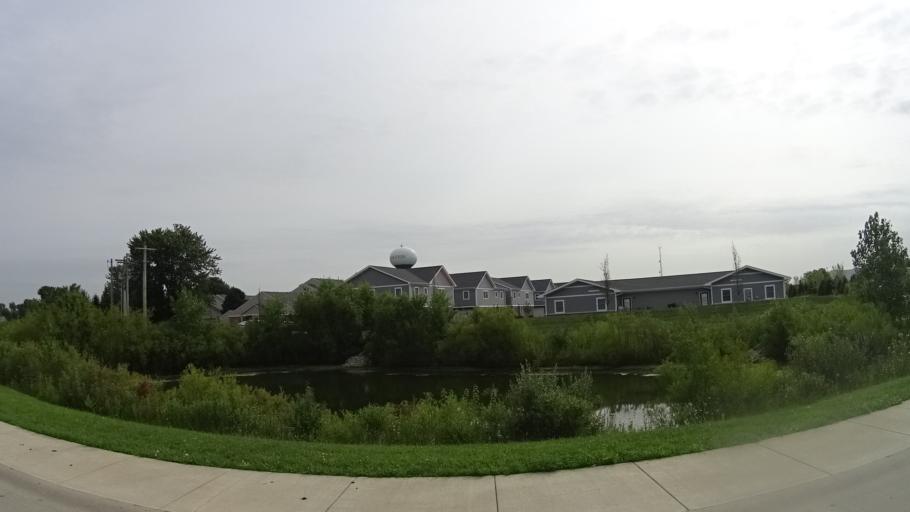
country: US
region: Indiana
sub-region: Madison County
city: Pendleton
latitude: 39.9998
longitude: -85.7708
